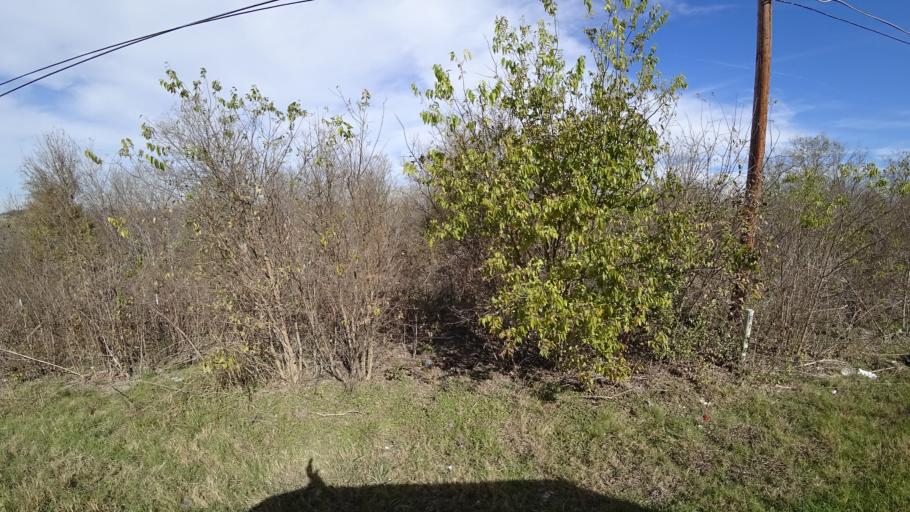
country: US
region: Texas
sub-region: Travis County
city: Onion Creek
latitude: 30.1178
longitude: -97.7082
